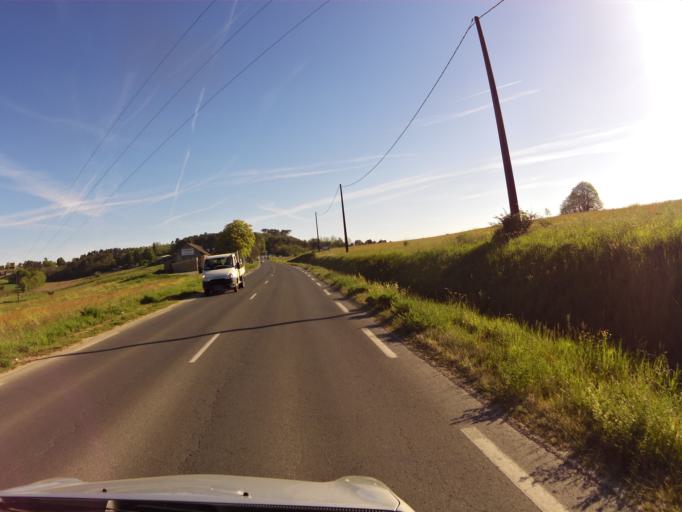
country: FR
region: Aquitaine
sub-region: Departement de la Dordogne
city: Sarlat-la-Caneda
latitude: 44.9324
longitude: 1.2084
